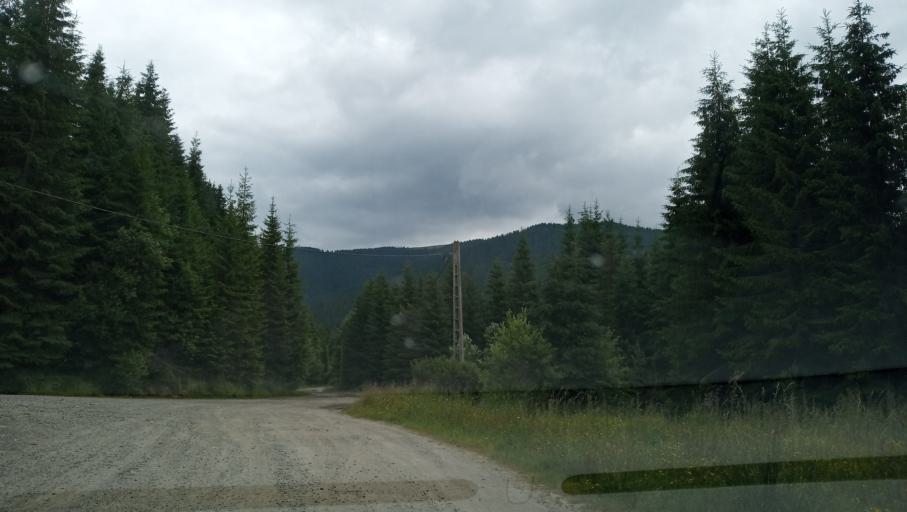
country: RO
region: Valcea
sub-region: Comuna Voineasa
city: Voineasa
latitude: 45.4257
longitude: 23.7589
